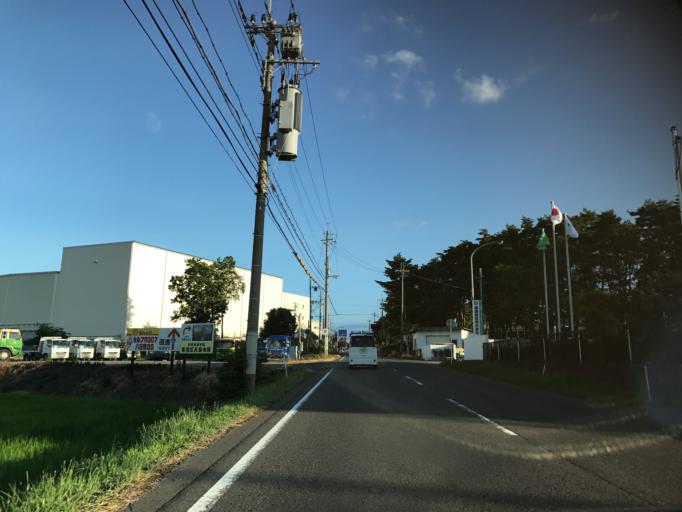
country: JP
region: Shiga Prefecture
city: Youkaichi
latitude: 35.0908
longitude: 136.2499
